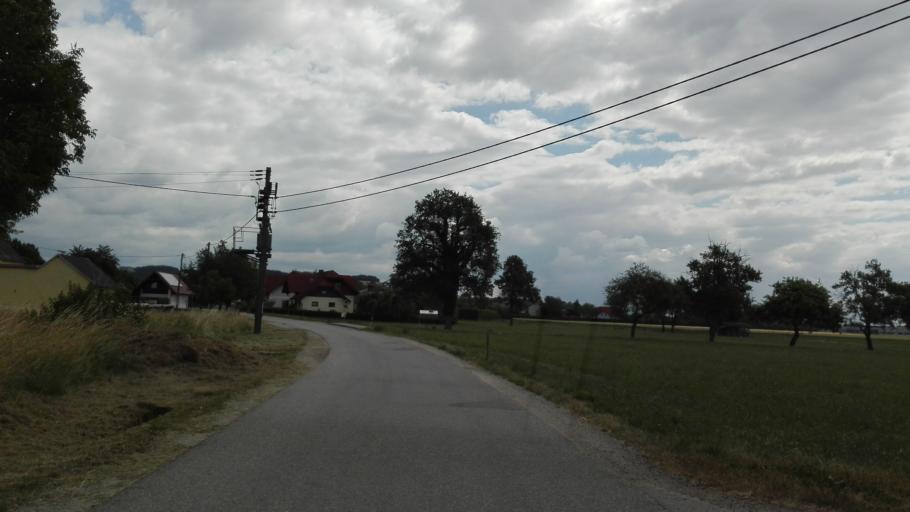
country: AT
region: Upper Austria
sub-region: Politischer Bezirk Perg
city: Perg
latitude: 48.2566
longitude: 14.5695
